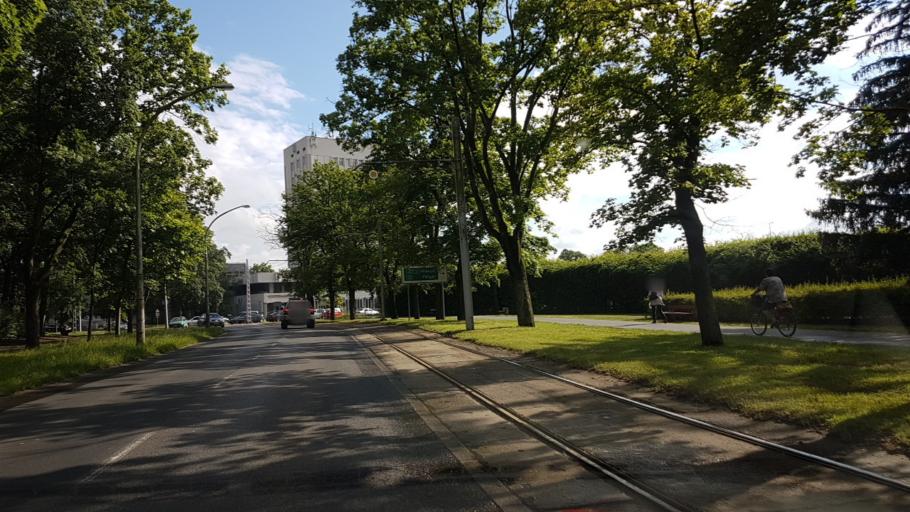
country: HU
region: Hajdu-Bihar
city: Debrecen
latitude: 47.5527
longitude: 21.6229
